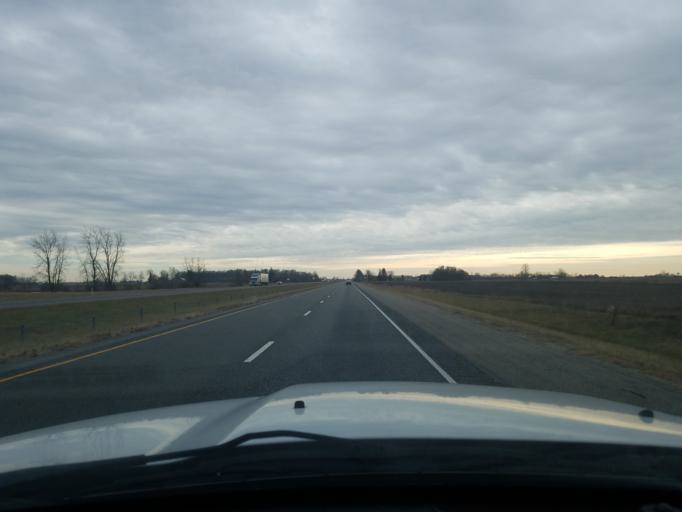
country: US
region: Indiana
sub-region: Grant County
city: Upland
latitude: 40.3965
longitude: -85.5489
